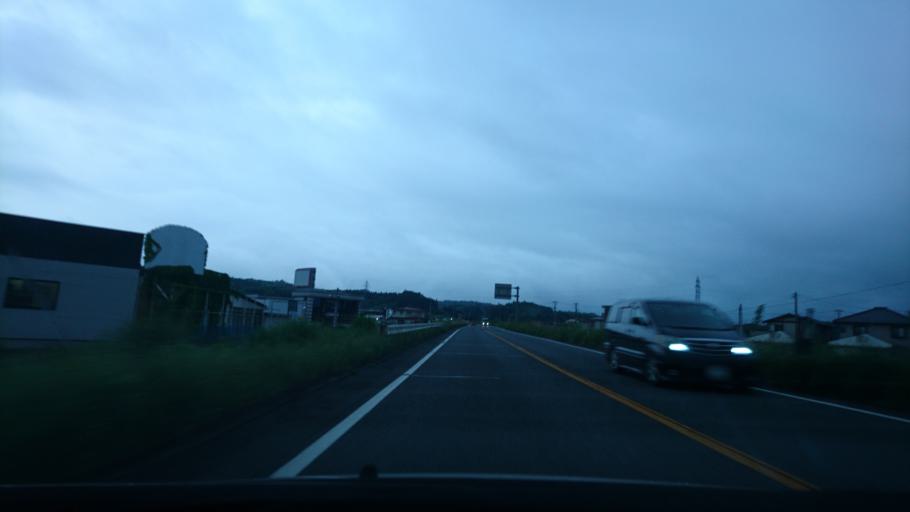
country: JP
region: Iwate
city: Ichinoseki
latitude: 38.9201
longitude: 141.1096
